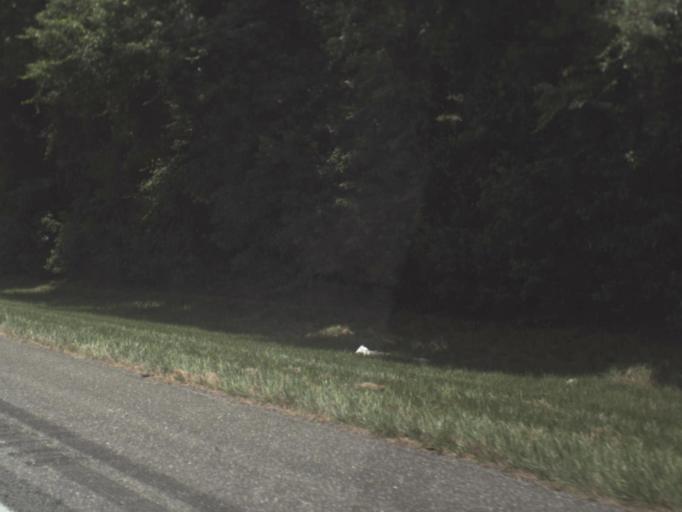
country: US
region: Florida
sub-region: Jefferson County
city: Monticello
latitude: 30.4442
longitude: -83.6761
